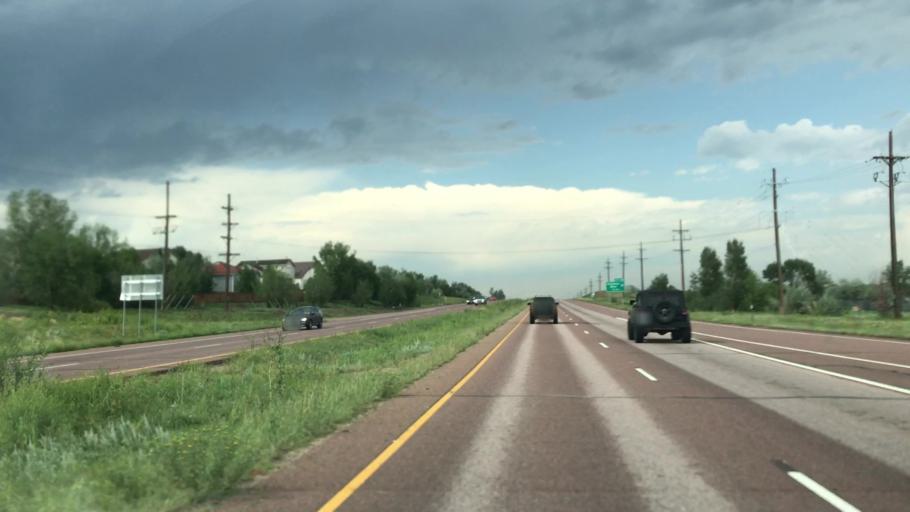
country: US
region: Colorado
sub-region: El Paso County
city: Fort Carson
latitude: 38.7522
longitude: -104.8113
